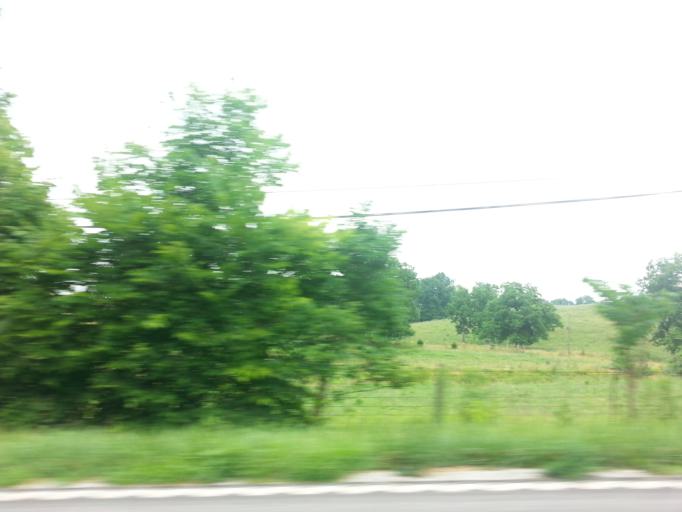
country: US
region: Kentucky
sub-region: Harrison County
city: Cynthiana
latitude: 38.4386
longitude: -84.2486
